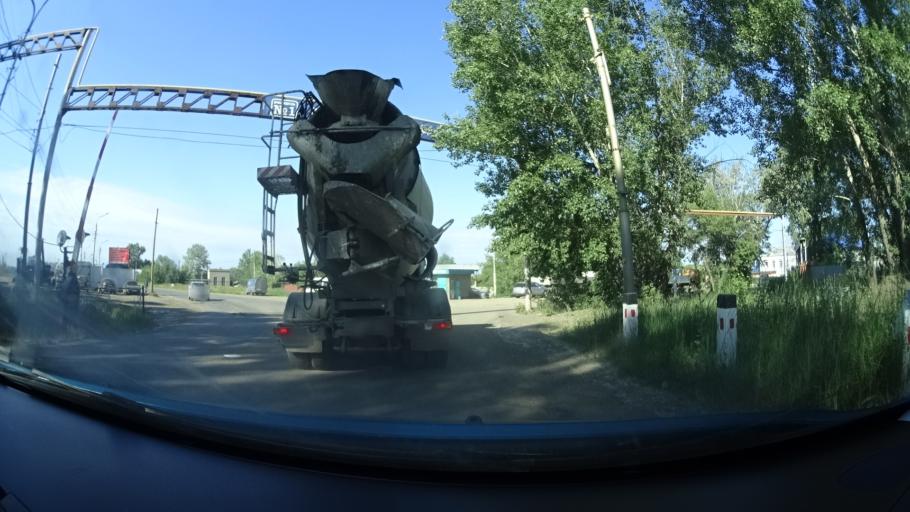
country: RU
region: Bashkortostan
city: Ufa
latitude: 54.8541
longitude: 56.0856
